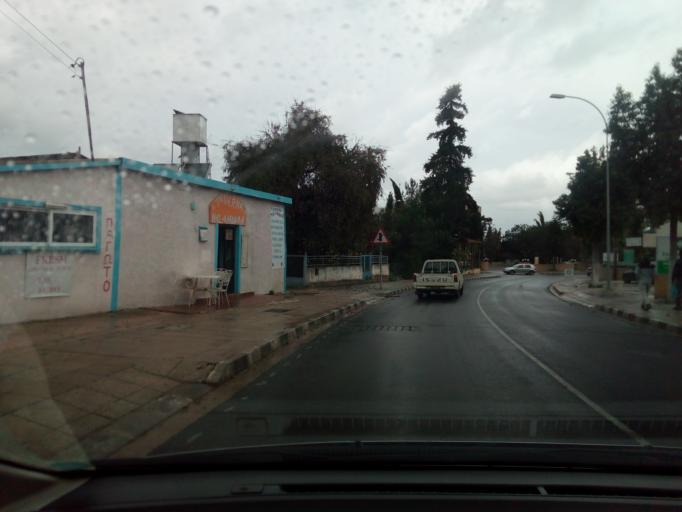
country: CY
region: Pafos
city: Polis
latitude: 35.0335
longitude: 32.4272
